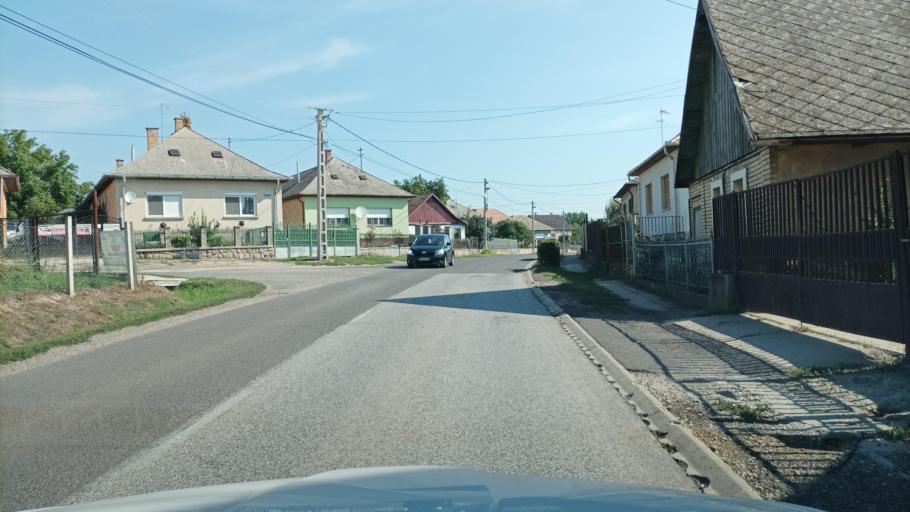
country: HU
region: Pest
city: Valko
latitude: 47.5658
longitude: 19.5171
